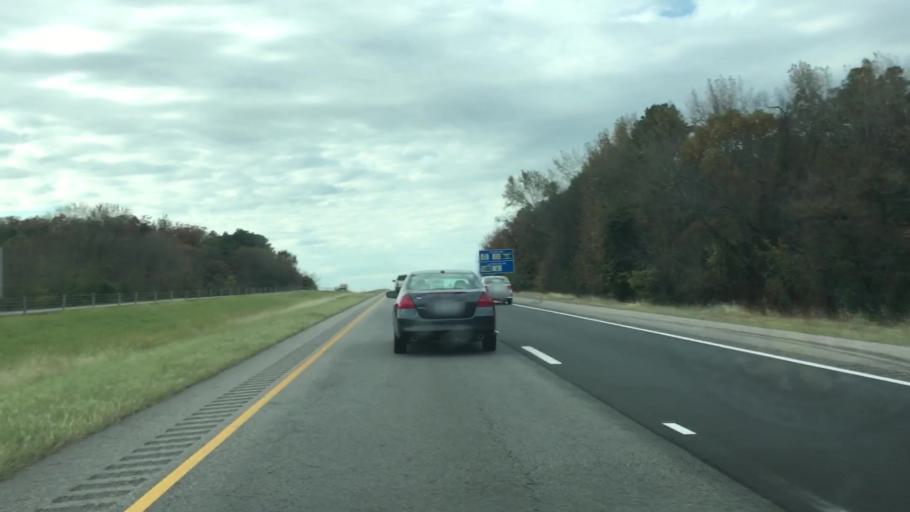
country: US
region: Arkansas
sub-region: Conway County
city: Morrilton
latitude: 35.1695
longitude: -92.6922
